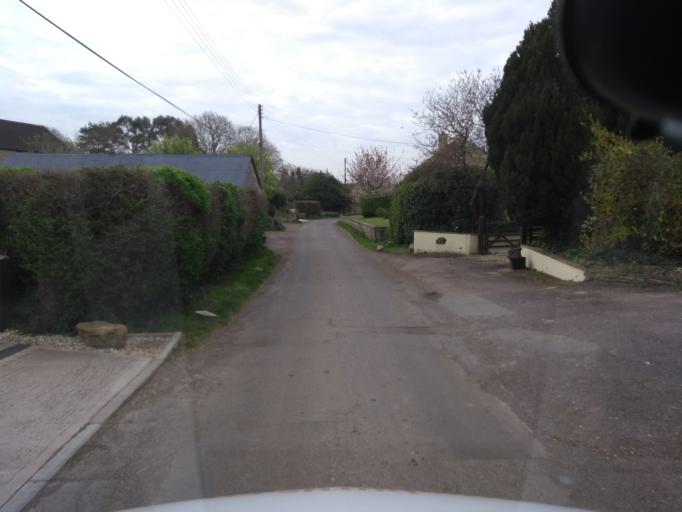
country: GB
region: England
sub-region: Somerset
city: Ilminster
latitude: 50.9800
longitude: -2.9657
